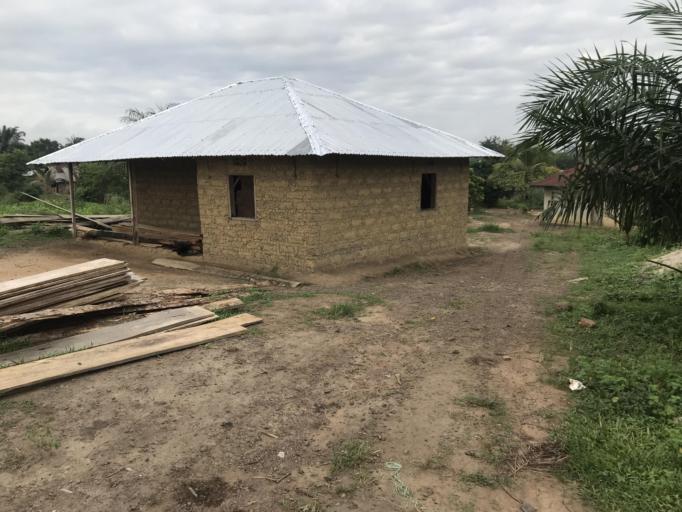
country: SL
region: Eastern Province
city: Pendembu
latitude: 8.0895
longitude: -10.6920
